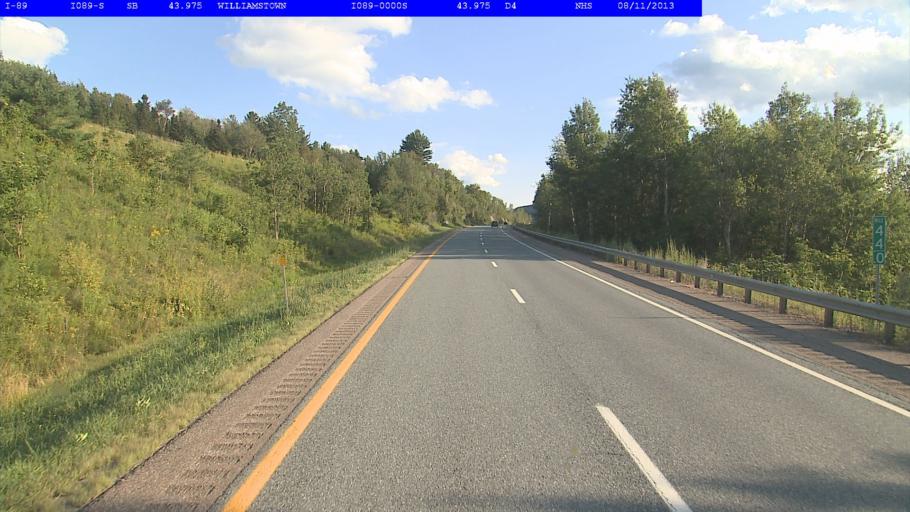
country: US
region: Vermont
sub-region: Washington County
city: Northfield
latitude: 44.1293
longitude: -72.6016
